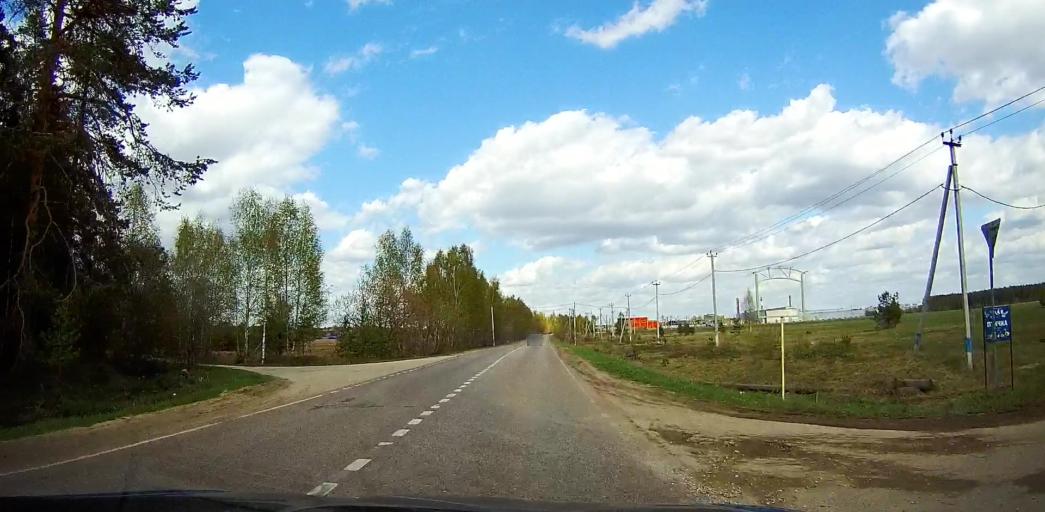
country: RU
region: Moskovskaya
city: Davydovo
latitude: 55.5985
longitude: 38.8401
